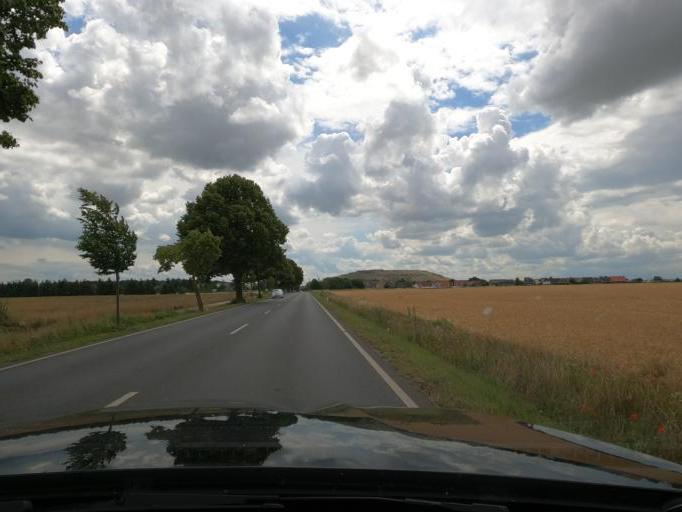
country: DE
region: Lower Saxony
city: Sehnde
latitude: 52.3282
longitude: 9.9514
